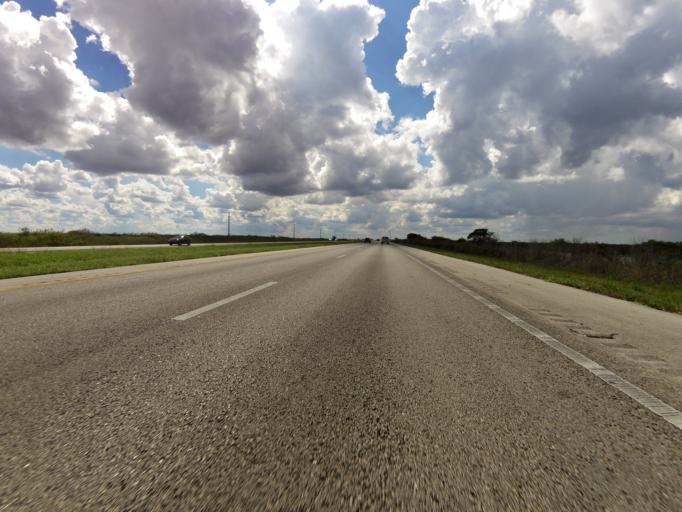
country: US
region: Florida
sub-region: Broward County
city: Weston
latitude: 26.1542
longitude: -80.7483
